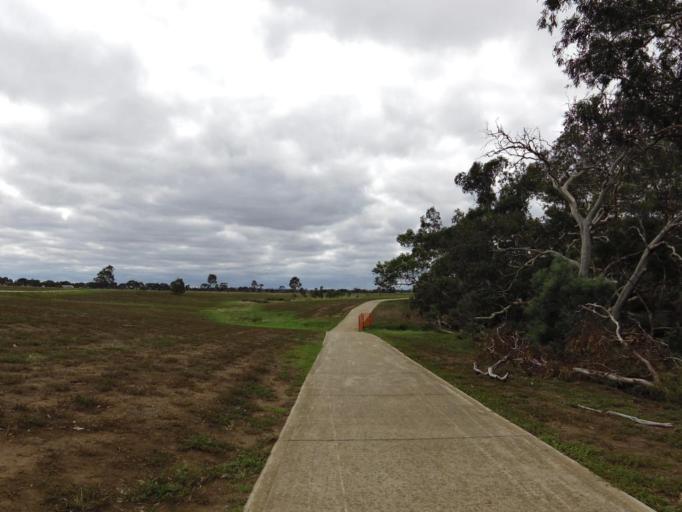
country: AU
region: Victoria
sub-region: Wyndham
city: Tarneit
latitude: -37.8817
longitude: 144.6397
